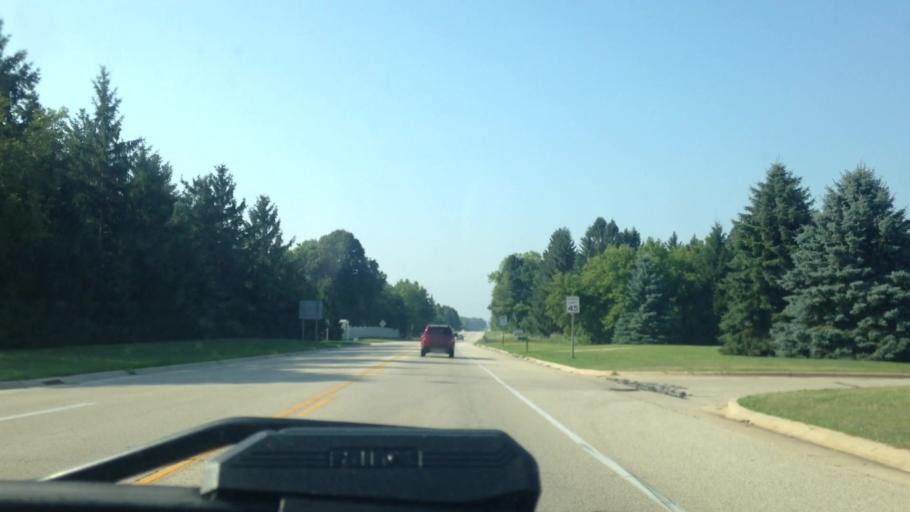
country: US
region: Wisconsin
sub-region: Washington County
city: Slinger
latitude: 43.3239
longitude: -88.2608
